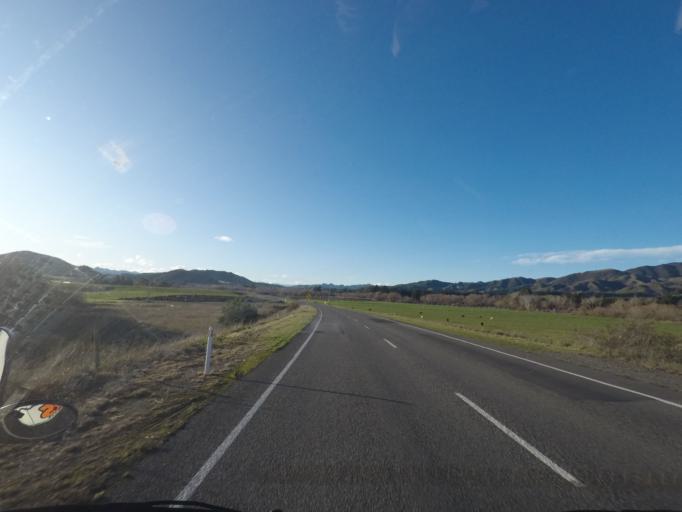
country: NZ
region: Canterbury
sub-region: Kaikoura District
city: Kaikoura
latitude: -42.7010
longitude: 173.3030
